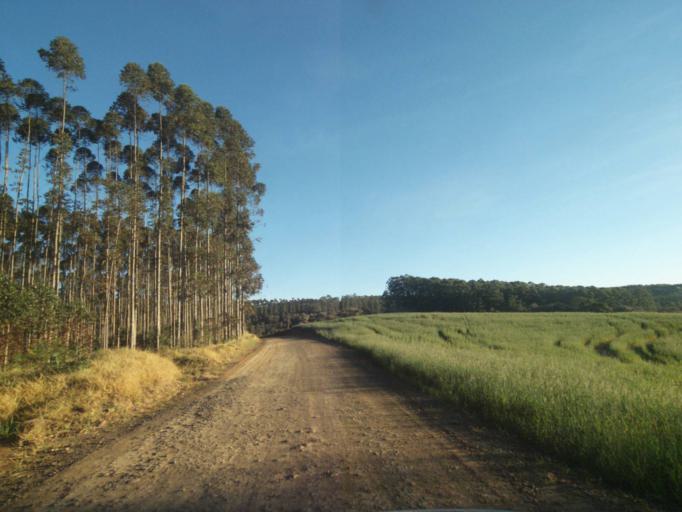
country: BR
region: Parana
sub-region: Telemaco Borba
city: Telemaco Borba
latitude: -24.4881
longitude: -50.5939
